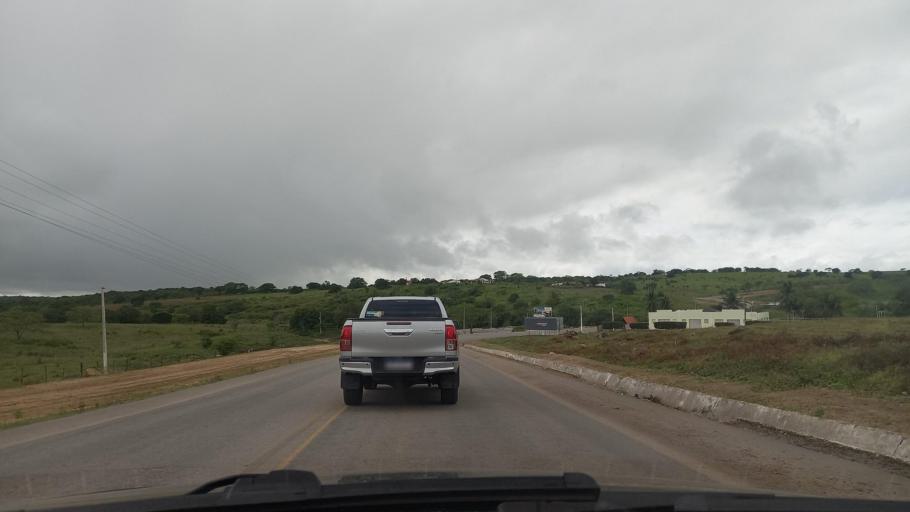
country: BR
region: Alagoas
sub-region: Batalha
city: Batalha
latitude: -9.6317
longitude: -37.2027
